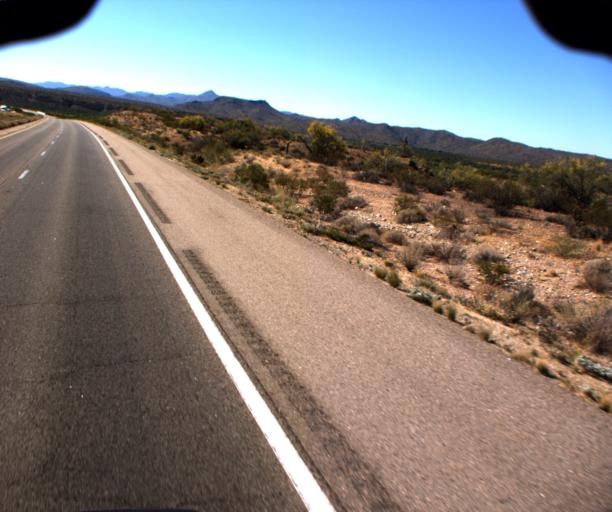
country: US
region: Arizona
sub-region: Yavapai County
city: Bagdad
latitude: 34.6483
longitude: -113.5706
